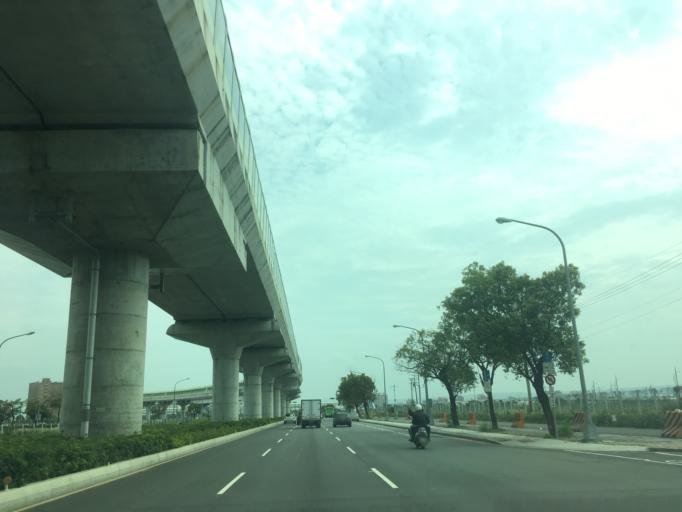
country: TW
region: Taiwan
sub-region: Taichung City
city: Taichung
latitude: 24.1281
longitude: 120.6463
